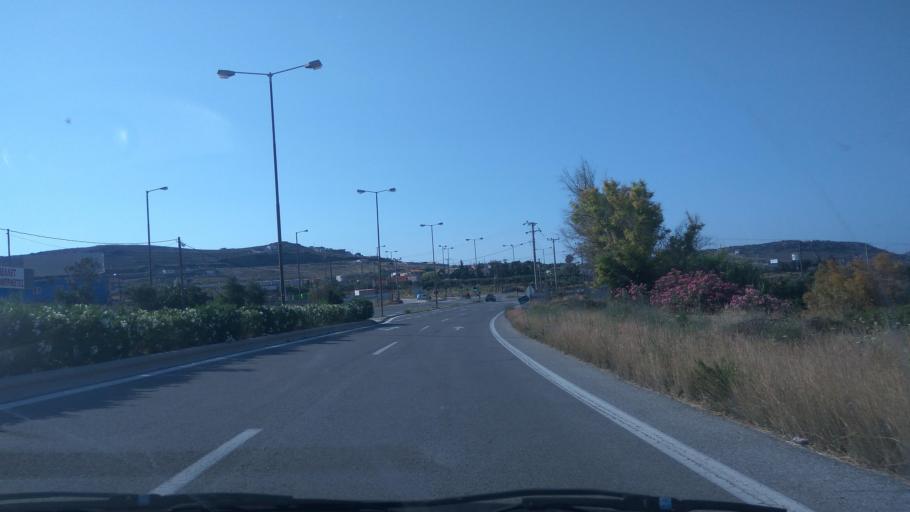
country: GR
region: Attica
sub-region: Nomarchia Anatolikis Attikis
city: Lavrio
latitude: 37.7934
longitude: 24.0555
